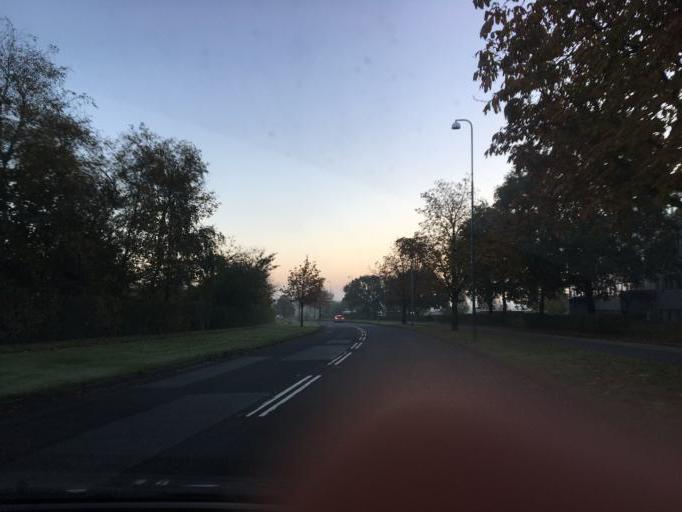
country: DK
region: South Denmark
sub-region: Vejle Kommune
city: Vejle
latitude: 55.6827
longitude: 9.5292
